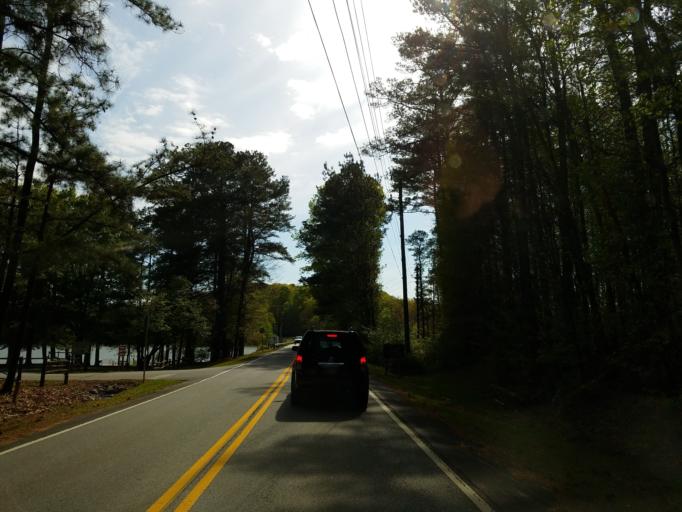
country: US
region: Georgia
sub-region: Douglas County
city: Lithia Springs
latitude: 33.7631
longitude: -84.6376
